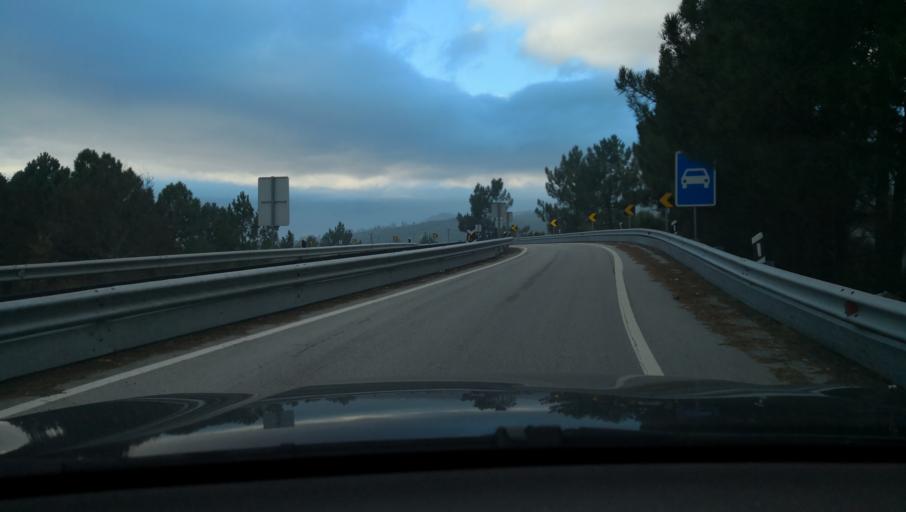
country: PT
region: Vila Real
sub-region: Vila Real
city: Vila Real
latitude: 41.3294
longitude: -7.6722
